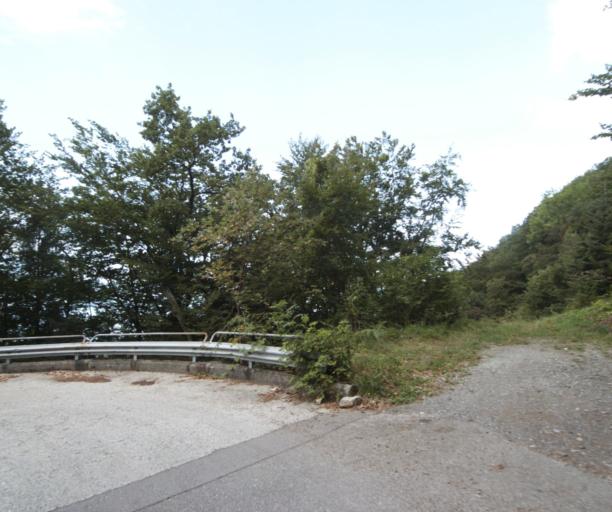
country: CH
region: Vaud
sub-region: Aigle District
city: Villeneuve
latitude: 46.4080
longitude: 6.9377
